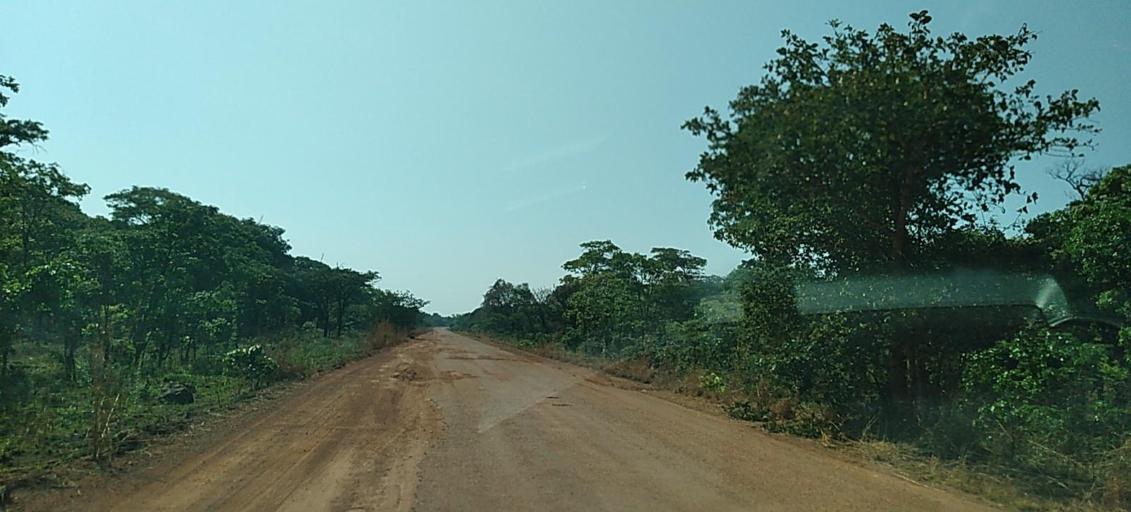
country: ZM
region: North-Western
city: Mwinilunga
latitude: -11.9167
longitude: 25.3092
